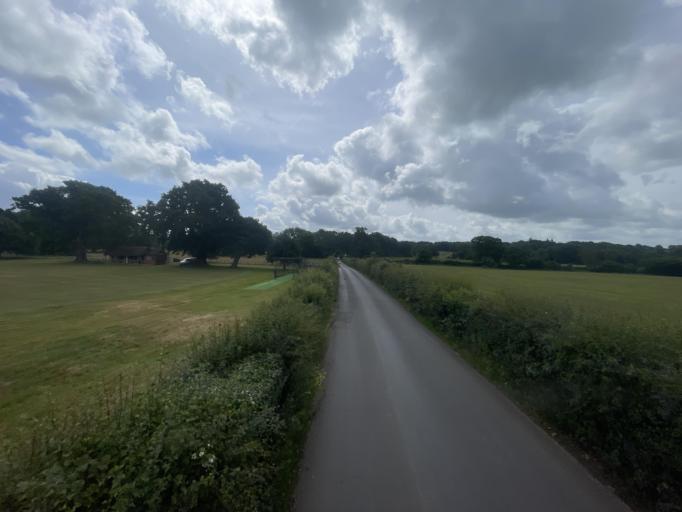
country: GB
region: England
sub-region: Kent
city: Edenbridge
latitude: 51.1587
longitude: 0.1485
